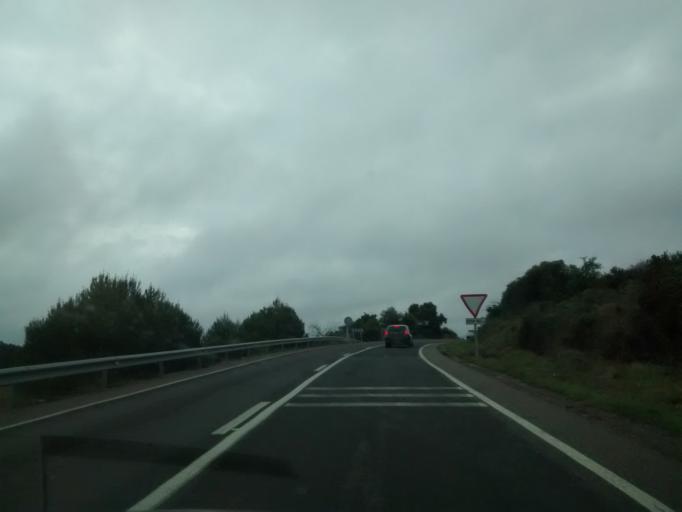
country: ES
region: Catalonia
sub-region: Provincia de Tarragona
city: Bot
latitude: 41.0515
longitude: 0.3651
